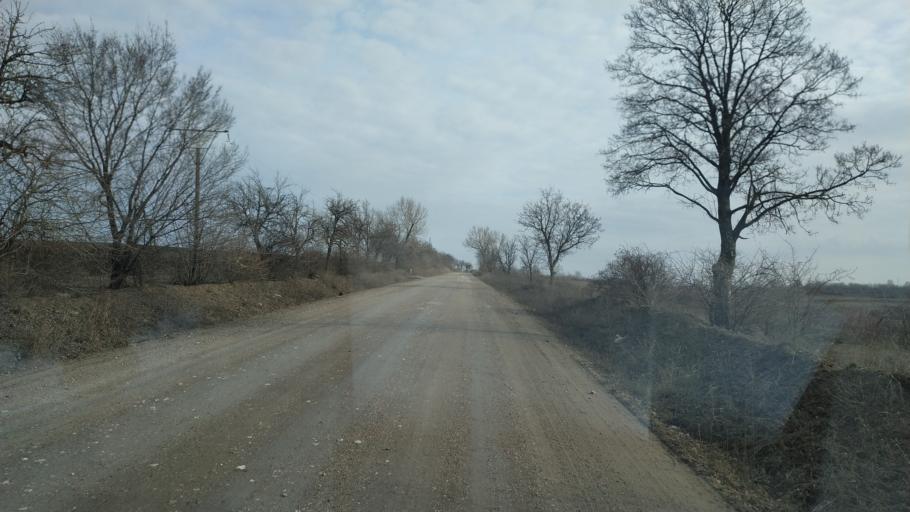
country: MD
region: Chisinau
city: Vadul lui Voda
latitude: 46.9881
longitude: 29.0904
